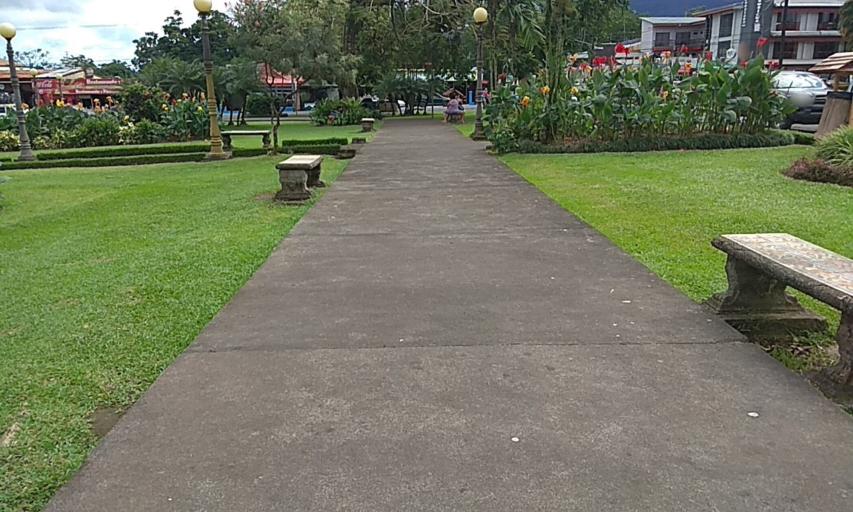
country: CR
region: Alajuela
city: La Fortuna
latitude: 10.4719
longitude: -84.6454
